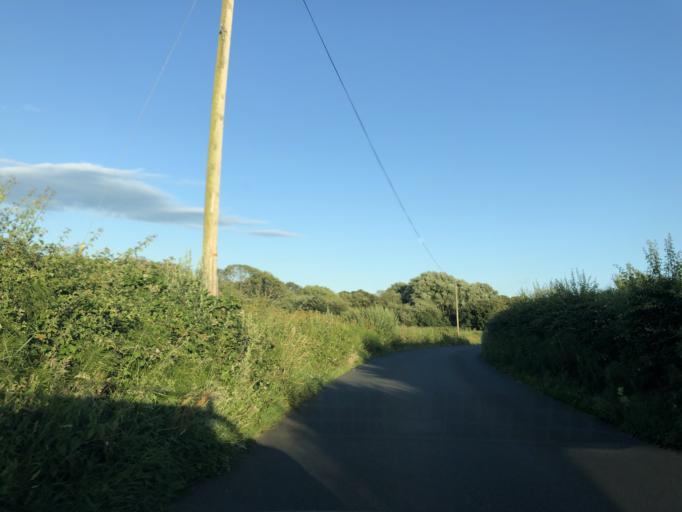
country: GB
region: England
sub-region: Isle of Wight
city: Chale
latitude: 50.6328
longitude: -1.3260
